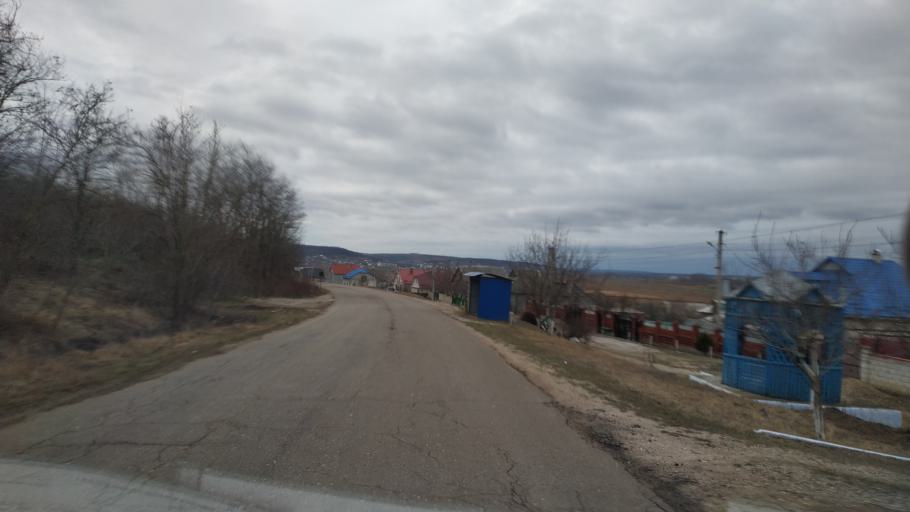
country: MD
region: Causeni
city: Causeni
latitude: 46.6635
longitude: 29.4503
